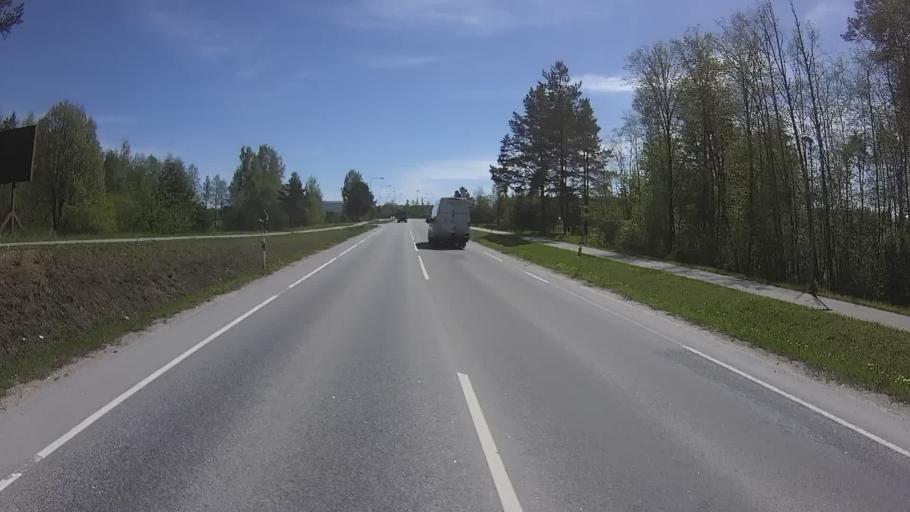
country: EE
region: Vorumaa
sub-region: Voru linn
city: Voru
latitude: 57.8179
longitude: 27.0263
